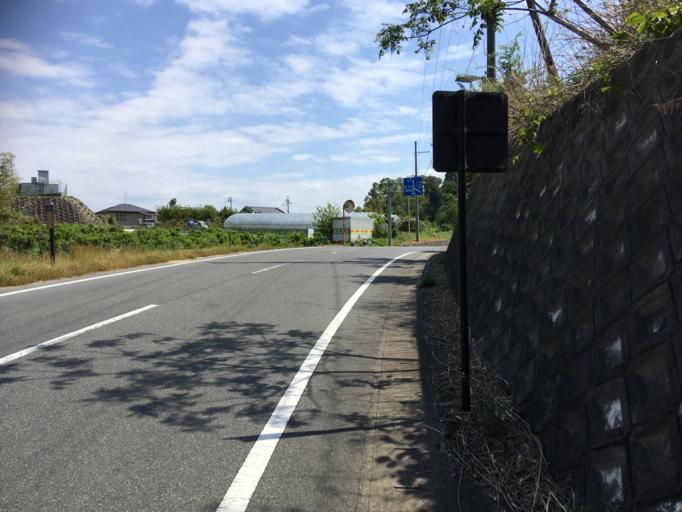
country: JP
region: Nara
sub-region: Ikoma-shi
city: Ikoma
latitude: 34.6350
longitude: 135.6777
